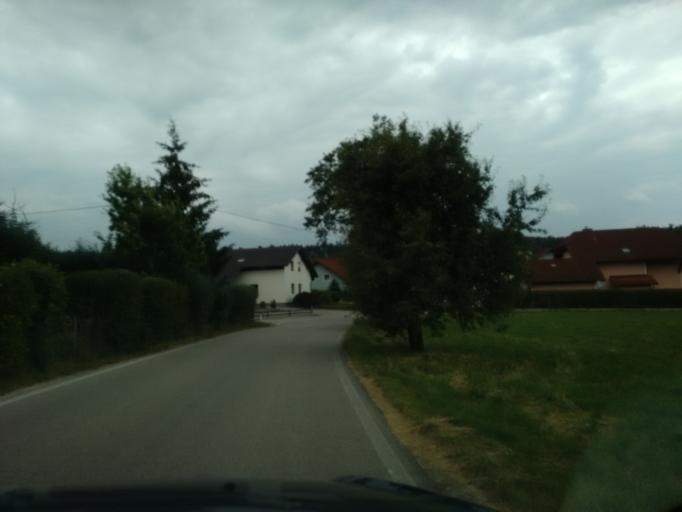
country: AT
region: Upper Austria
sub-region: Politischer Bezirk Grieskirchen
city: Bad Schallerbach
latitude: 48.1935
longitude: 13.9685
